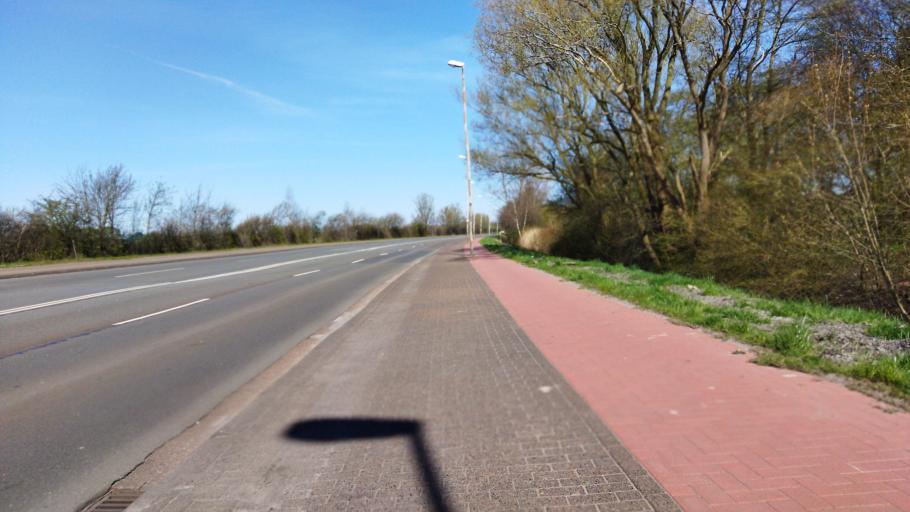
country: DE
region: Lower Saxony
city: Nordenham
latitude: 53.5175
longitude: 8.5103
